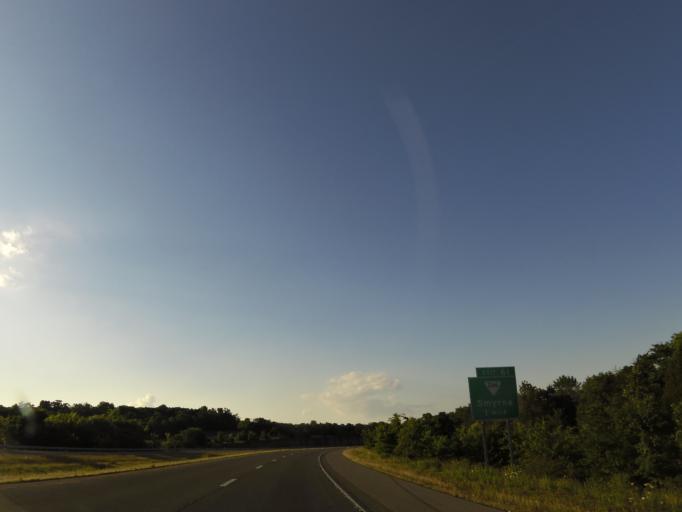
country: US
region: Tennessee
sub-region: Rutherford County
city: Smyrna
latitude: 35.9669
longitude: -86.4489
